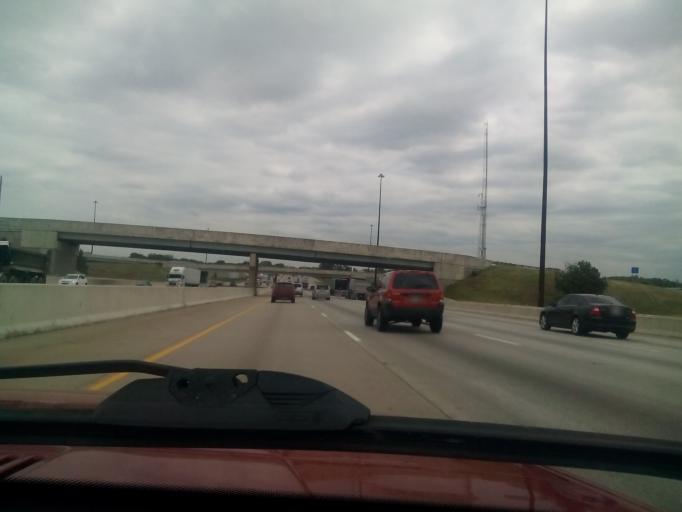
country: US
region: Indiana
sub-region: Lake County
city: Highland
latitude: 41.5741
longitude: -87.4644
